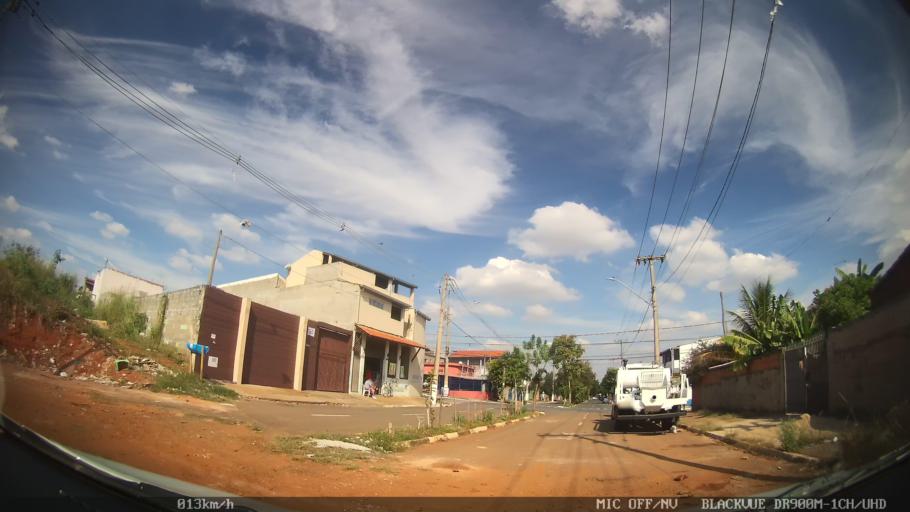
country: BR
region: Sao Paulo
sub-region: Hortolandia
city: Hortolandia
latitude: -22.8850
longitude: -47.2357
